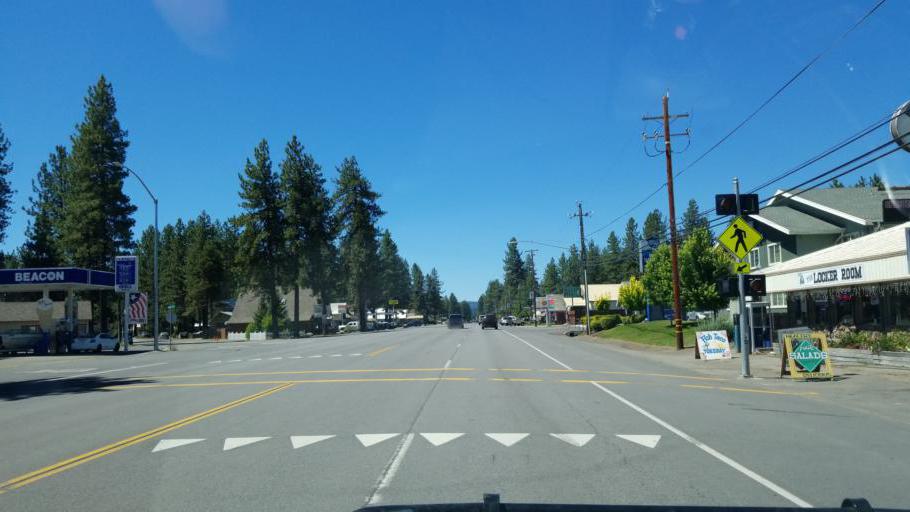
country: US
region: California
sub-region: Plumas County
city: Chester
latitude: 40.3067
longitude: -121.2318
